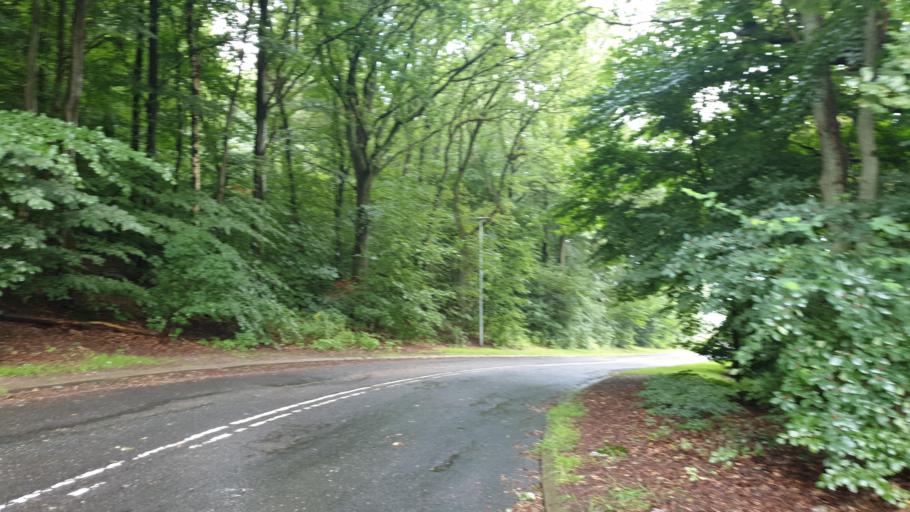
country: DK
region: Central Jutland
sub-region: Silkeborg Kommune
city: Silkeborg
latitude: 56.1907
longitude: 9.5445
